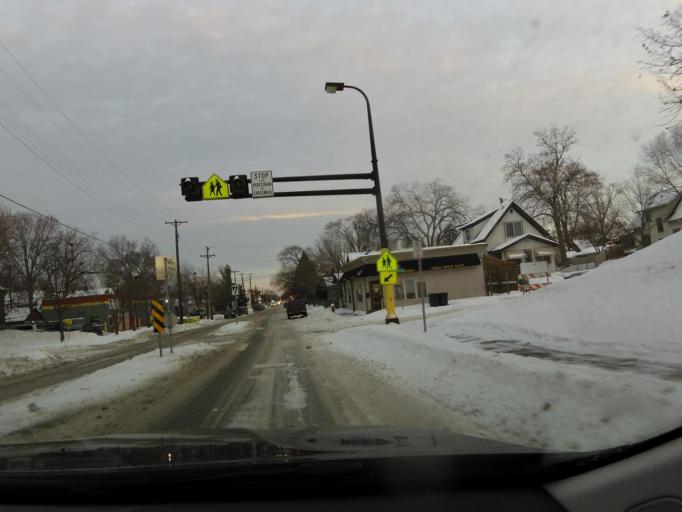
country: US
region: Minnesota
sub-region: Hennepin County
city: Minneapolis
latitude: 44.9341
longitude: -93.2554
